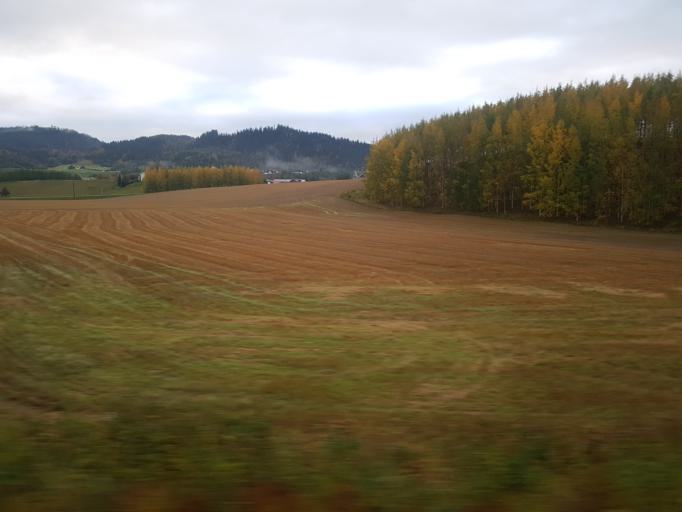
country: NO
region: Sor-Trondelag
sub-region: Melhus
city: Lundamo
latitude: 63.1950
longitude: 10.3052
